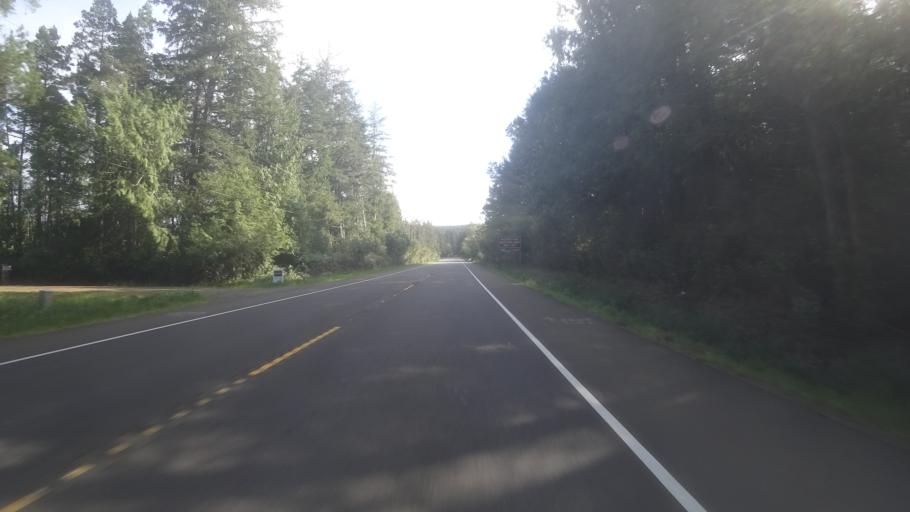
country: US
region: Oregon
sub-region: Lane County
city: Dunes City
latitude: 43.8883
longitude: -124.1201
